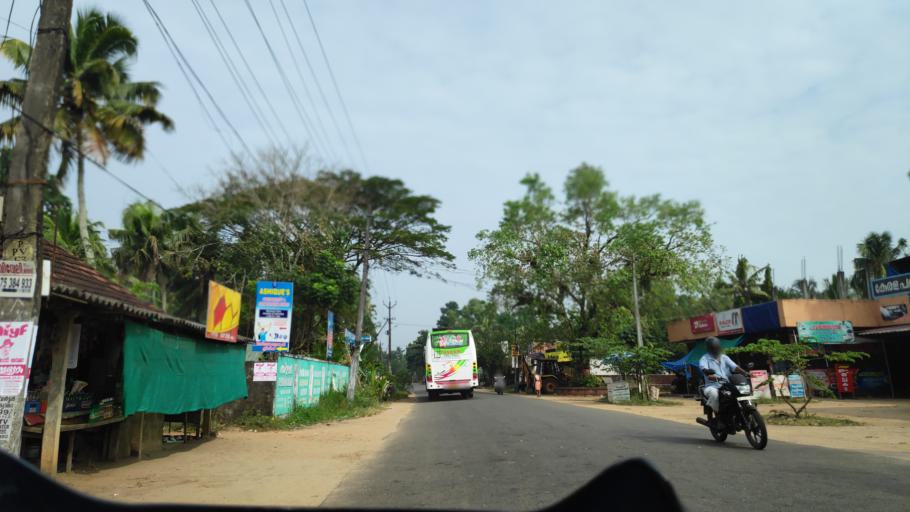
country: IN
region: Kerala
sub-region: Alappuzha
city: Kutiatodu
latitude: 9.8084
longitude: 76.3529
